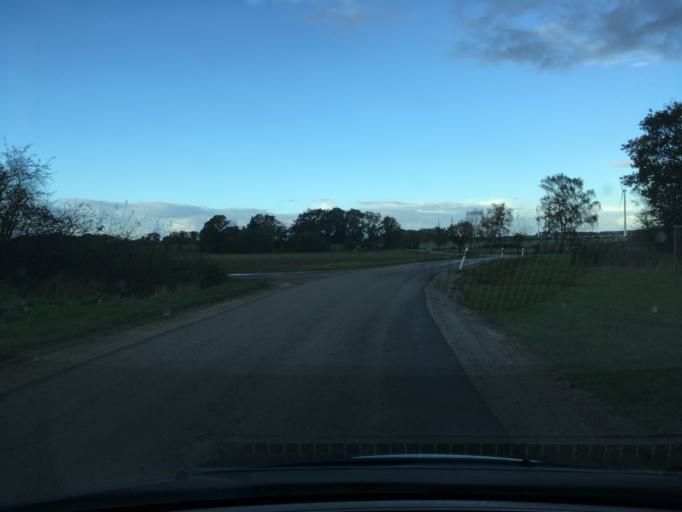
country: DE
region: Lower Saxony
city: Reinstorf
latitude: 53.2407
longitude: 10.5663
